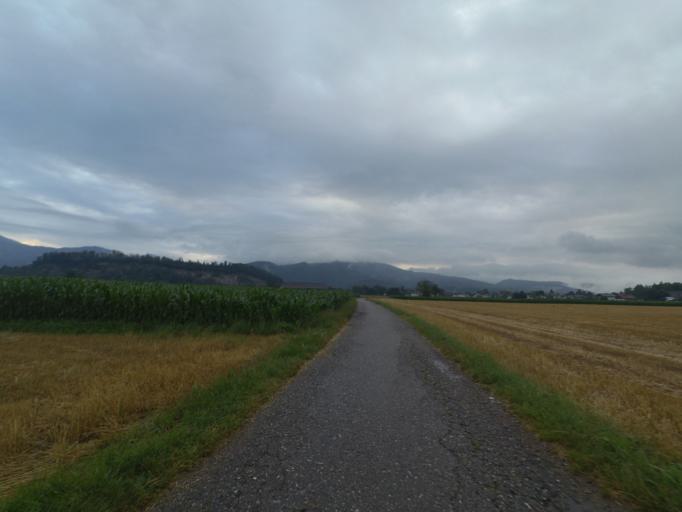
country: AT
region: Salzburg
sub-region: Politischer Bezirk Salzburg-Umgebung
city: Anif
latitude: 47.7536
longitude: 13.0538
